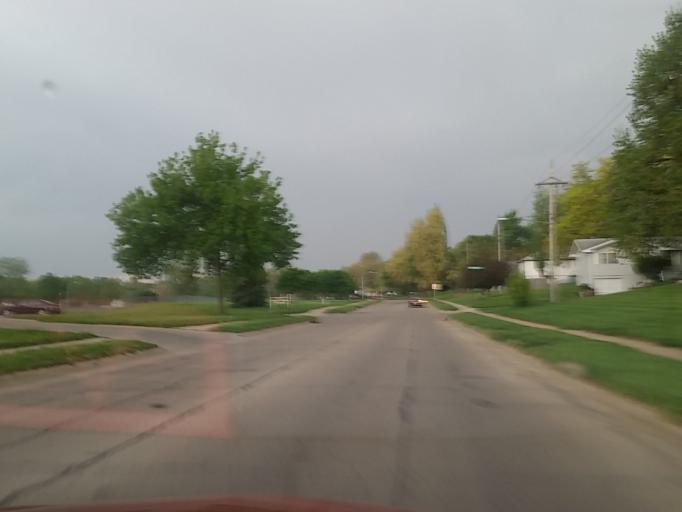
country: US
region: Nebraska
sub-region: Sarpy County
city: Offutt Air Force Base
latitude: 41.1473
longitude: -95.9198
